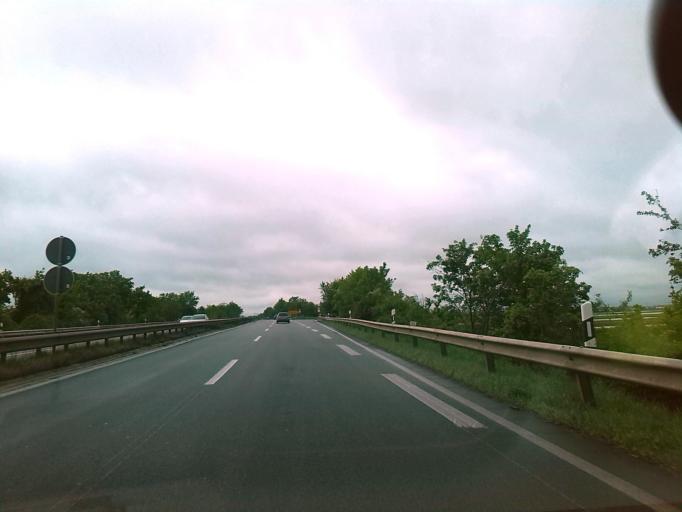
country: DE
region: Rheinland-Pfalz
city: Frankenthal
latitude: 49.5062
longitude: 8.3552
